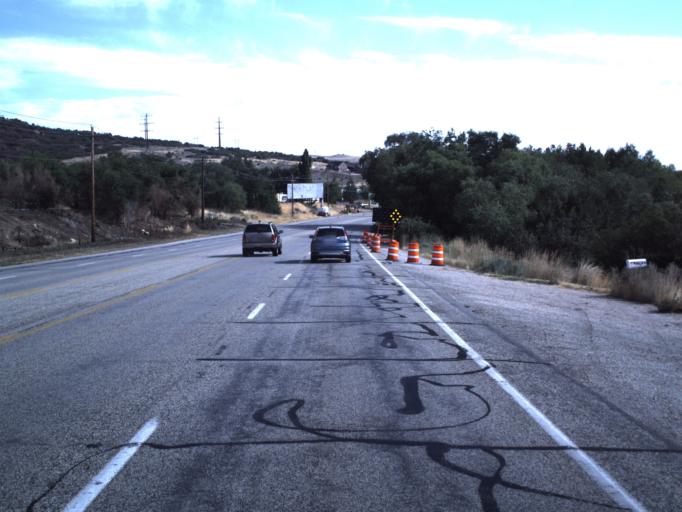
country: US
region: Utah
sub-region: Box Elder County
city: Willard
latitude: 41.3876
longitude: -112.0329
